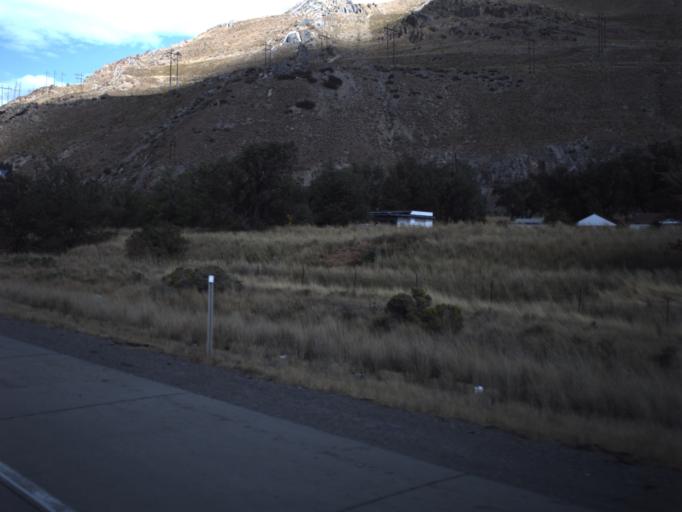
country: US
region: Utah
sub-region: Tooele County
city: Stansbury park
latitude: 40.7007
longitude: -112.2581
